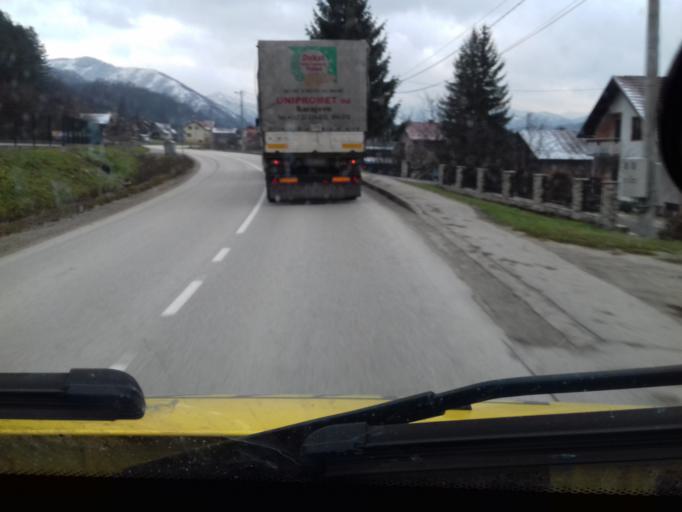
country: BA
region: Federation of Bosnia and Herzegovina
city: Zepce
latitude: 44.4233
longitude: 18.0549
